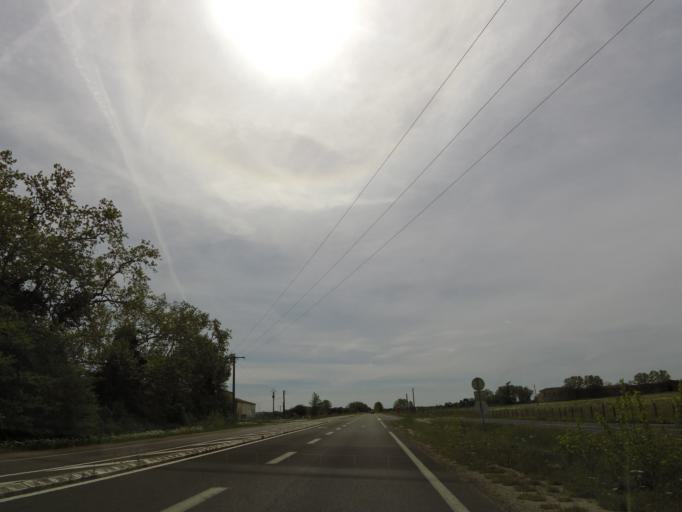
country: FR
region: Languedoc-Roussillon
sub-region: Departement de l'Herault
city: Saint-Just
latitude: 43.6526
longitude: 4.1388
